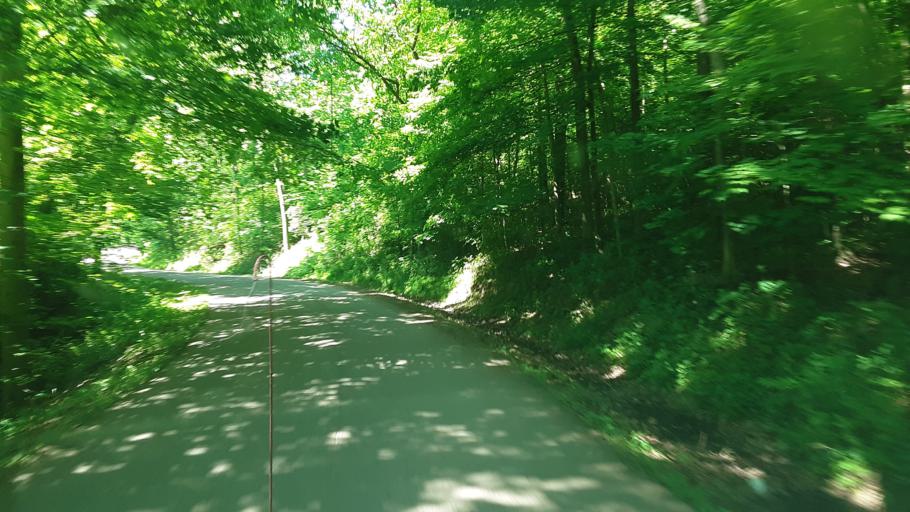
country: US
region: Ohio
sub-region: Tuscarawas County
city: Newcomerstown
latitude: 40.2207
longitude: -81.6692
